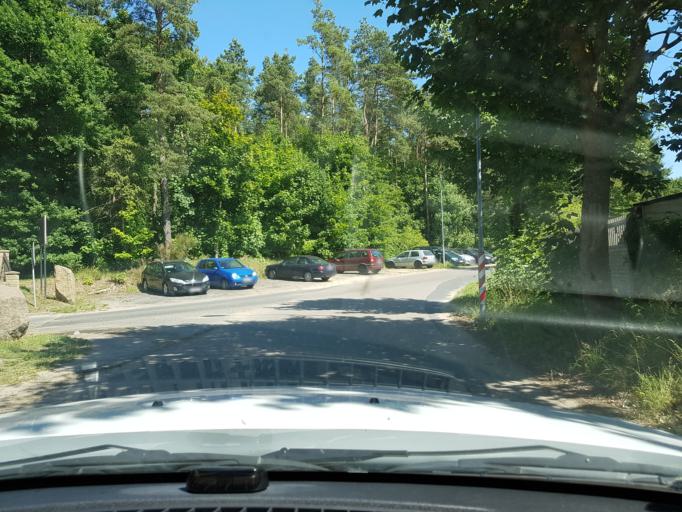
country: PL
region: West Pomeranian Voivodeship
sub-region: Powiat koszalinski
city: Mielno
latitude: 54.1721
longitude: 16.0824
